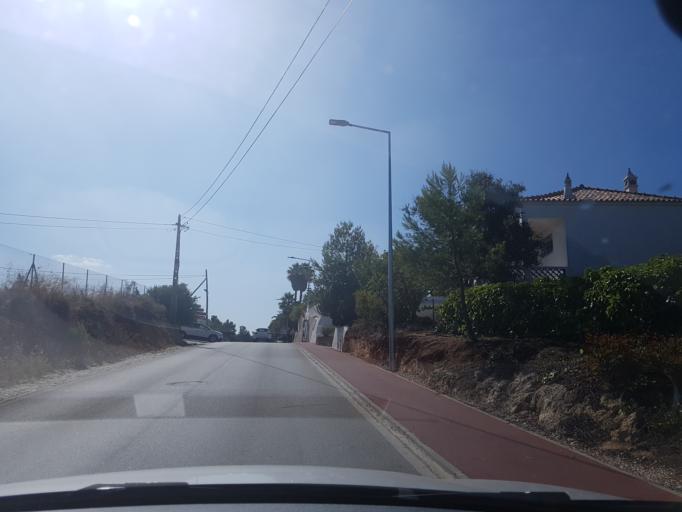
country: PT
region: Faro
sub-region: Lagoa
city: Carvoeiro
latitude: 37.0943
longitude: -8.4569
